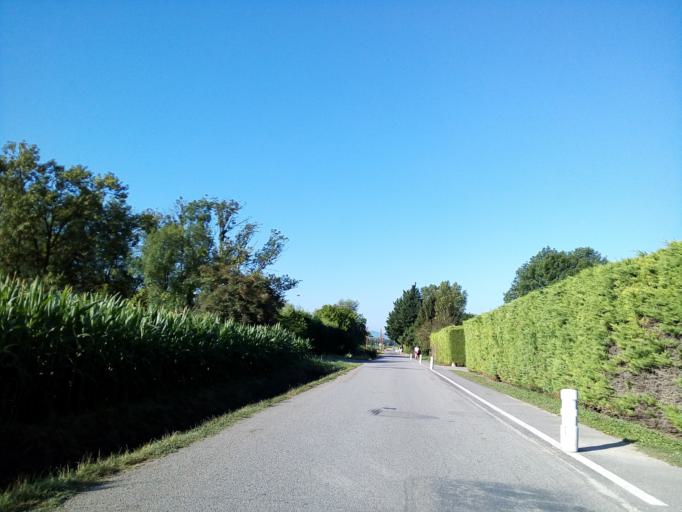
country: FR
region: Rhone-Alpes
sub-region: Departement de l'Isere
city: Lumbin
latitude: 45.3046
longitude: 5.9156
